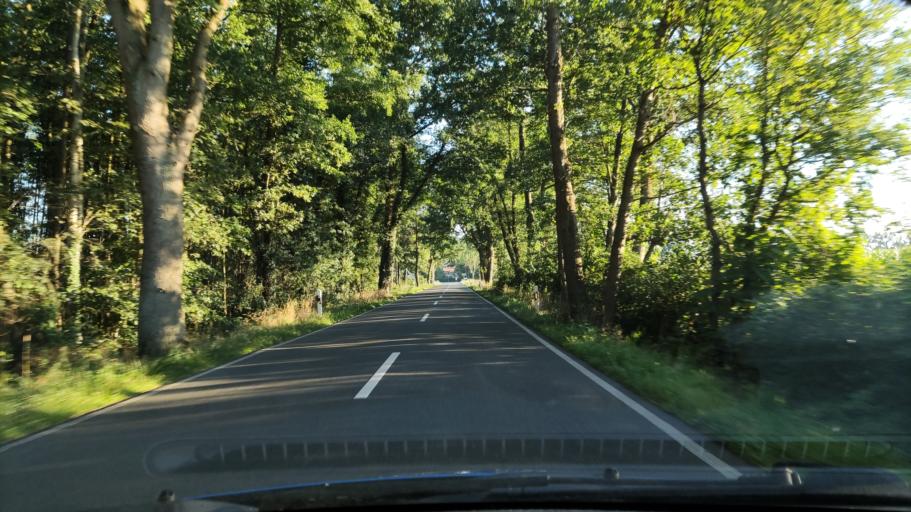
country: DE
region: Lower Saxony
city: Jameln
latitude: 53.0315
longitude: 11.1287
